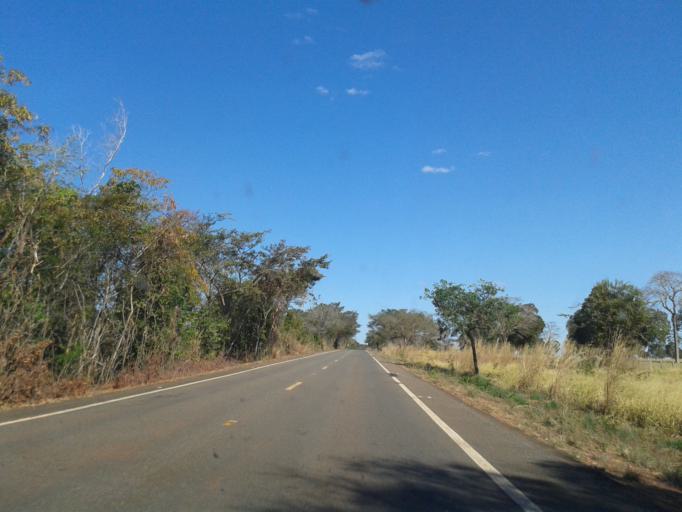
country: BR
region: Goias
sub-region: Sao Miguel Do Araguaia
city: Sao Miguel do Araguaia
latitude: -13.9207
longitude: -50.3228
